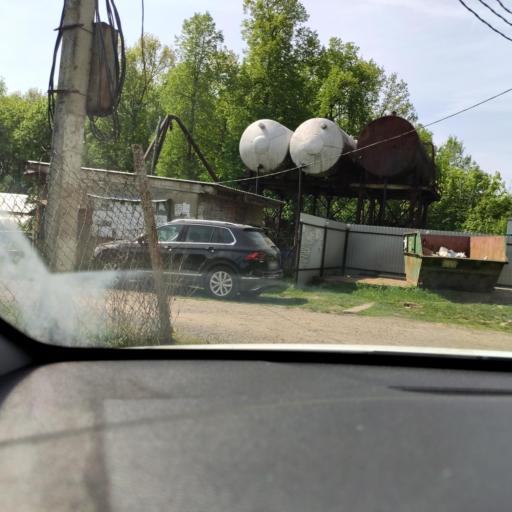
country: RU
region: Tatarstan
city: Sviyazhsk
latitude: 55.7479
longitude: 48.8081
